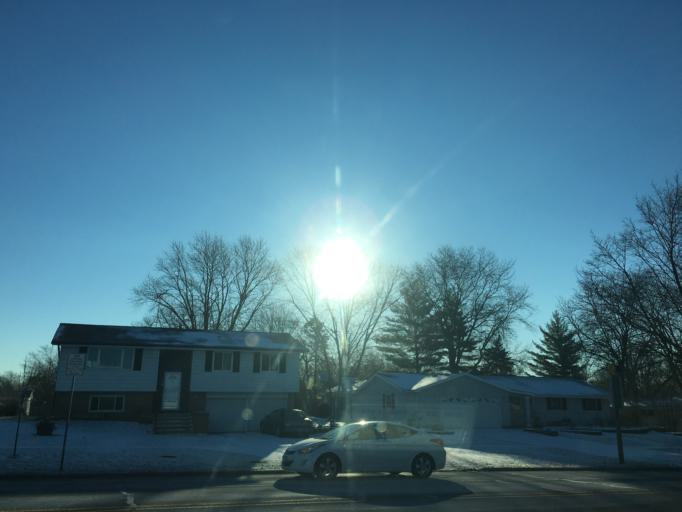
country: US
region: Illinois
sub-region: DuPage County
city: Hanover Park
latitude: 42.0197
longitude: -88.1192
